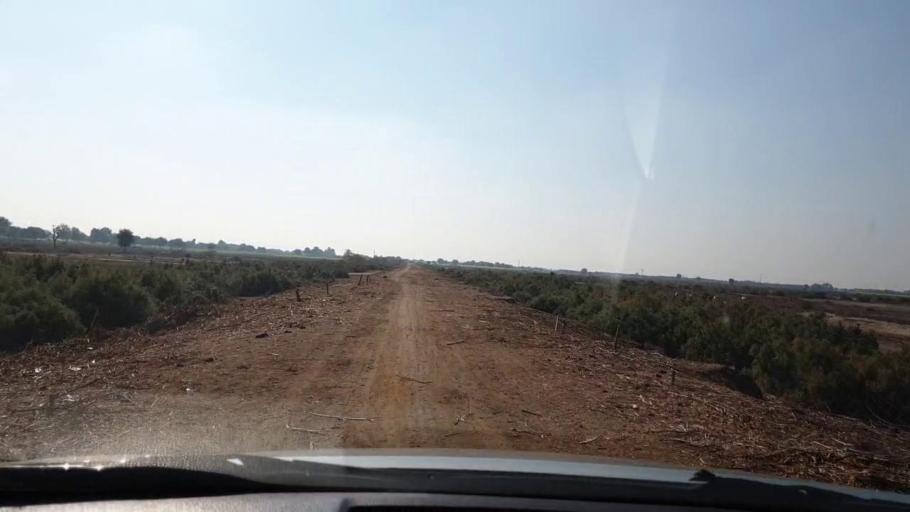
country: PK
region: Sindh
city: Jhol
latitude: 25.8751
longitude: 68.8952
